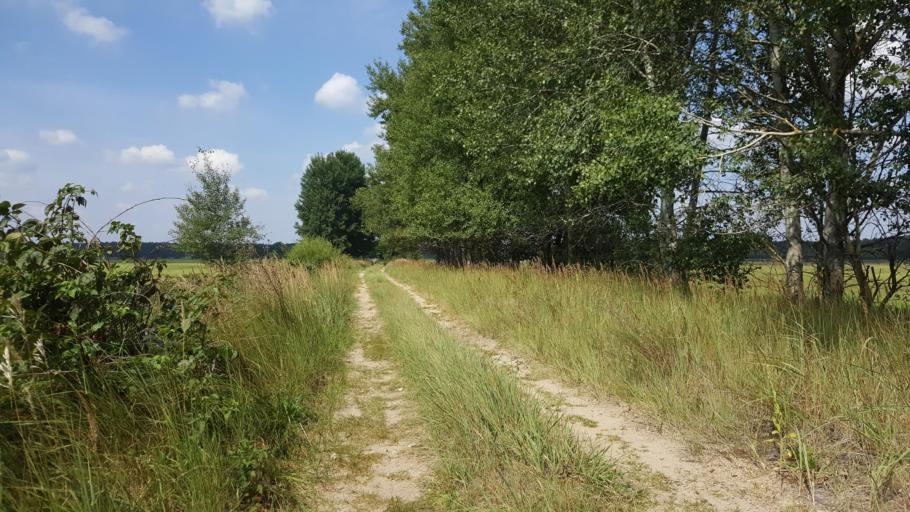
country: PL
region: Podlasie
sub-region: Powiat hajnowski
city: Hajnowka
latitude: 52.5758
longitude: 23.5825
